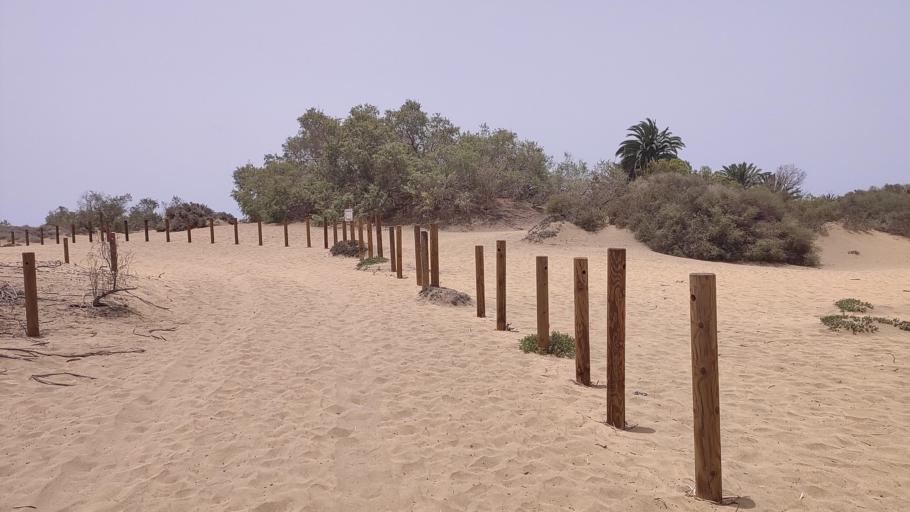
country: ES
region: Canary Islands
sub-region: Provincia de Las Palmas
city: Playa del Ingles
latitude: 27.7413
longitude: -15.5898
